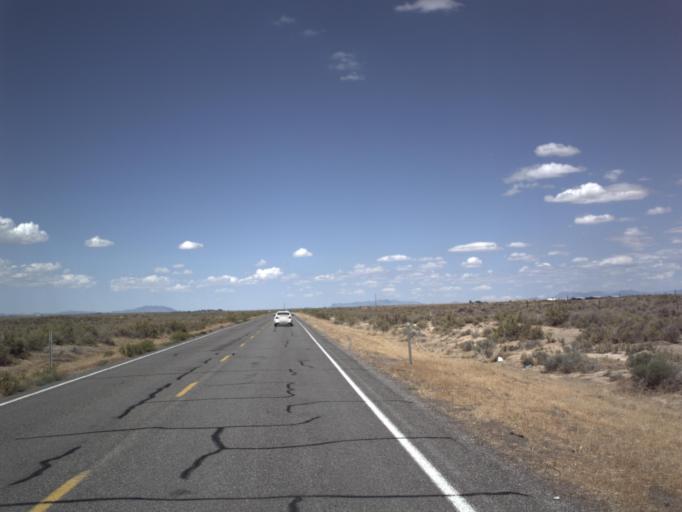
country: US
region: Utah
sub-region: Millard County
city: Delta
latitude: 39.3016
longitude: -112.4722
